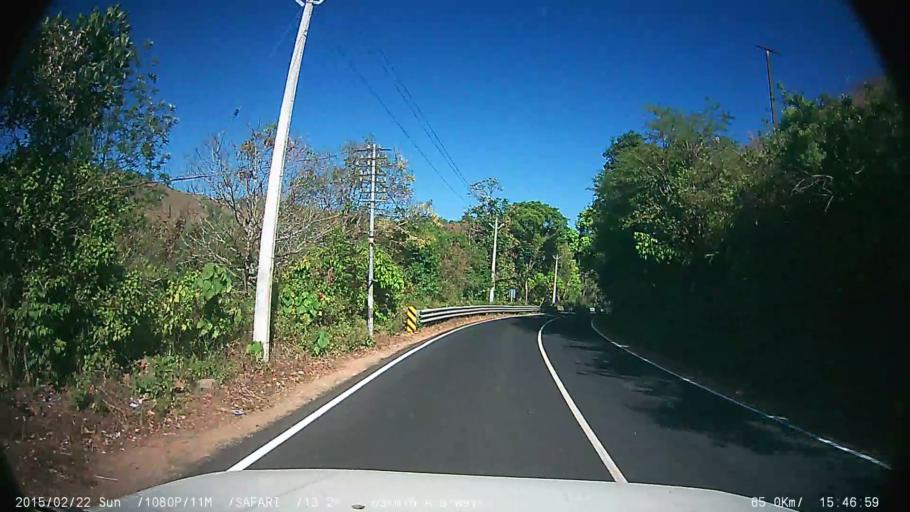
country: IN
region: Kerala
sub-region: Kottayam
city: Erattupetta
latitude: 9.5792
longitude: 76.9874
